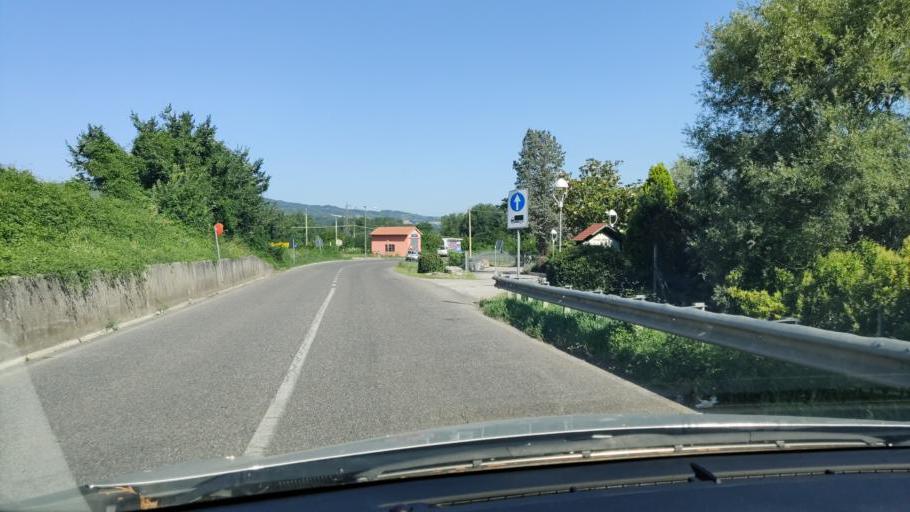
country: IT
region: Umbria
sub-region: Provincia di Perugia
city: Ponterio-Pian di Porto
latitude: 42.7957
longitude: 12.4114
